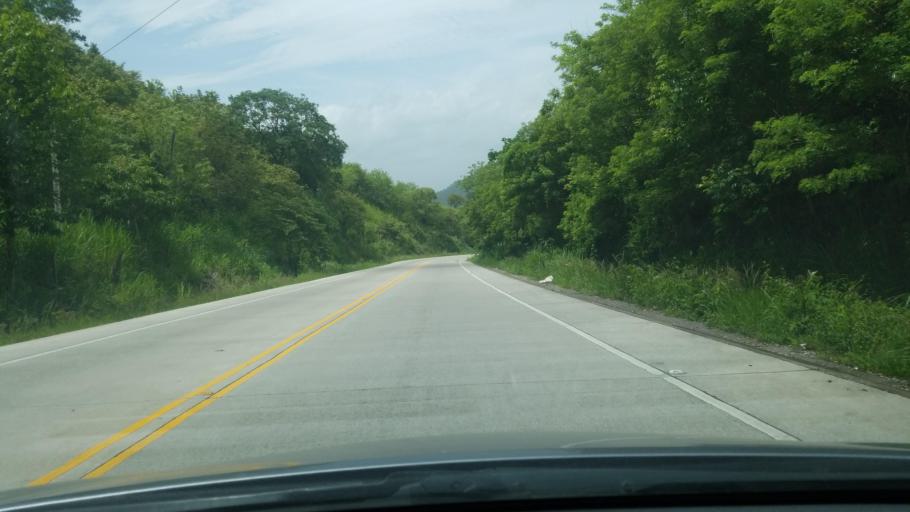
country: HN
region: Copan
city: Veracruz
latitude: 14.9110
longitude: -88.7525
